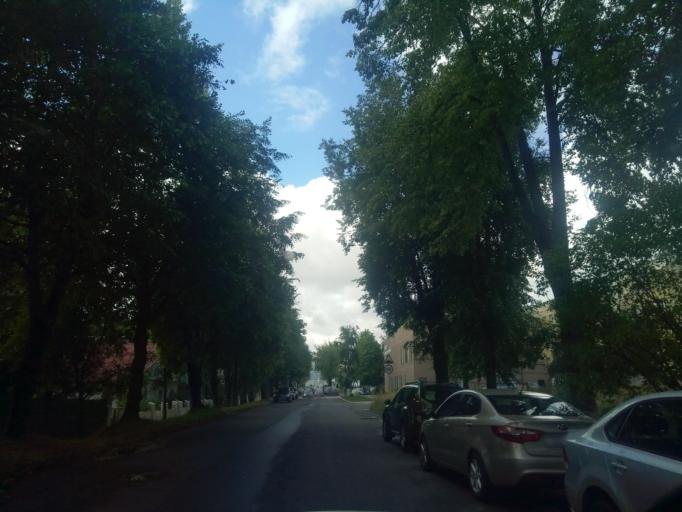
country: BY
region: Minsk
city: Novoye Medvezhino
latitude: 53.8833
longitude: 27.4995
